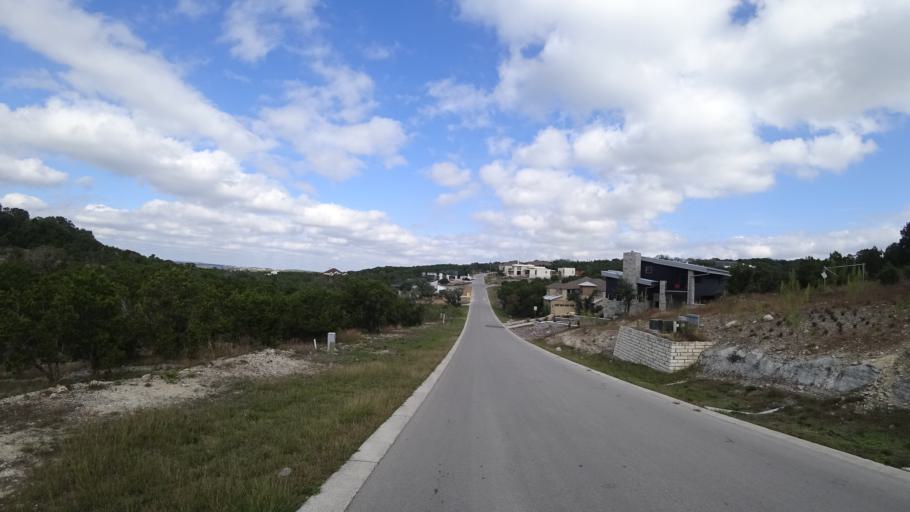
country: US
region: Texas
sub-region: Travis County
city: Bee Cave
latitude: 30.2515
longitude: -97.9275
